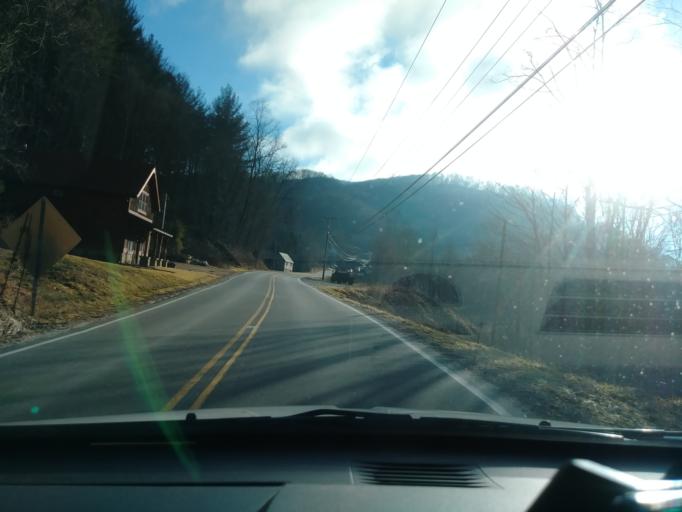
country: US
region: North Carolina
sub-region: Avery County
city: Banner Elk
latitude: 36.1727
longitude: -81.9148
